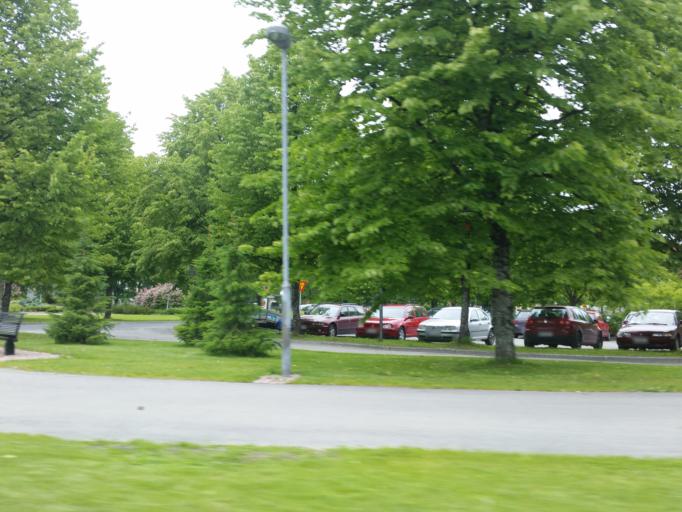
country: FI
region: Northern Savo
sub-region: Kuopio
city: Kuopio
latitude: 62.8866
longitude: 27.6791
